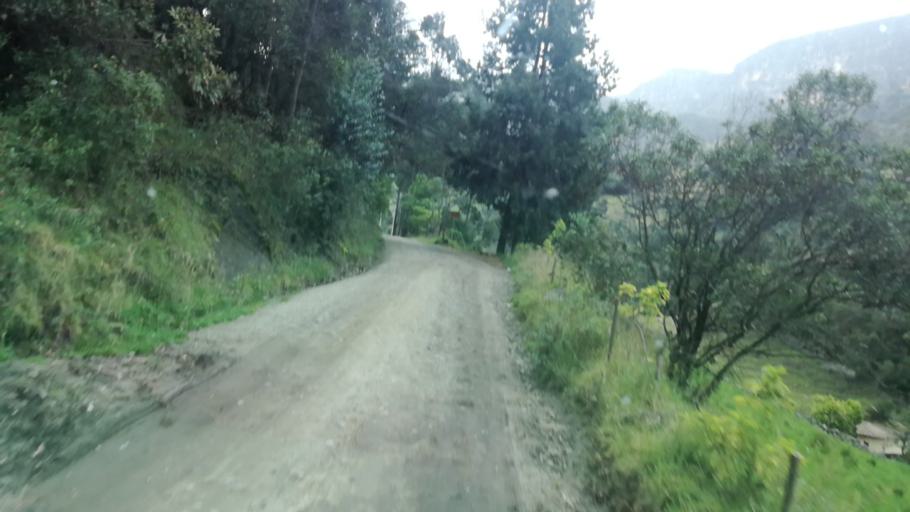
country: CO
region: Boyaca
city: Socha Viejo
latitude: 5.9406
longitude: -72.6890
